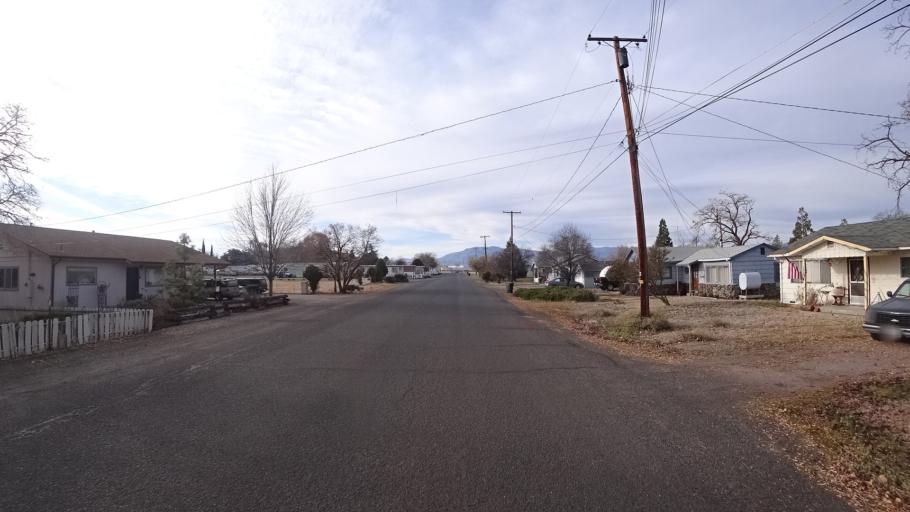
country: US
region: California
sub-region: Siskiyou County
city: Montague
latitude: 41.7264
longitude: -122.5322
